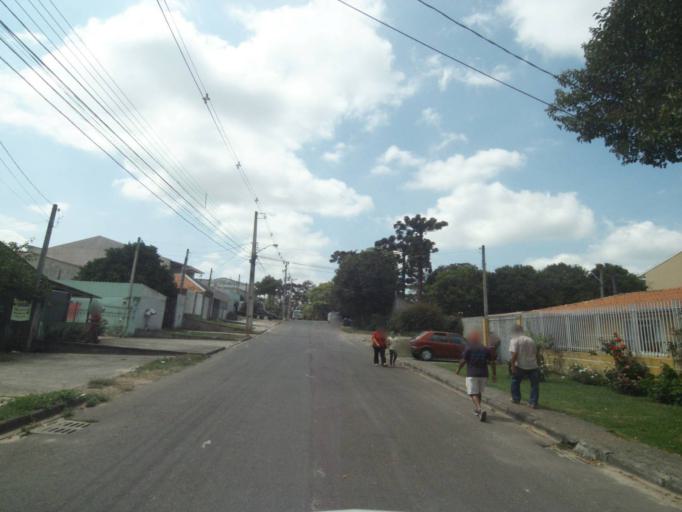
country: BR
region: Parana
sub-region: Sao Jose Dos Pinhais
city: Sao Jose dos Pinhais
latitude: -25.5467
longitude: -49.2509
